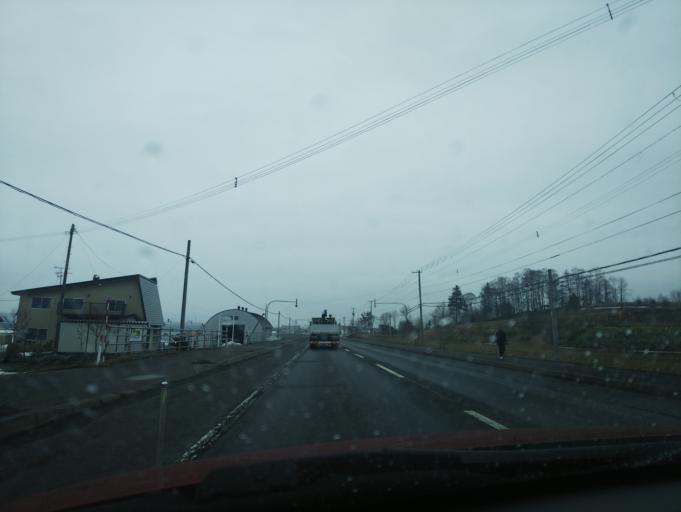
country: JP
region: Hokkaido
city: Nayoro
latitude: 44.1540
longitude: 142.3991
